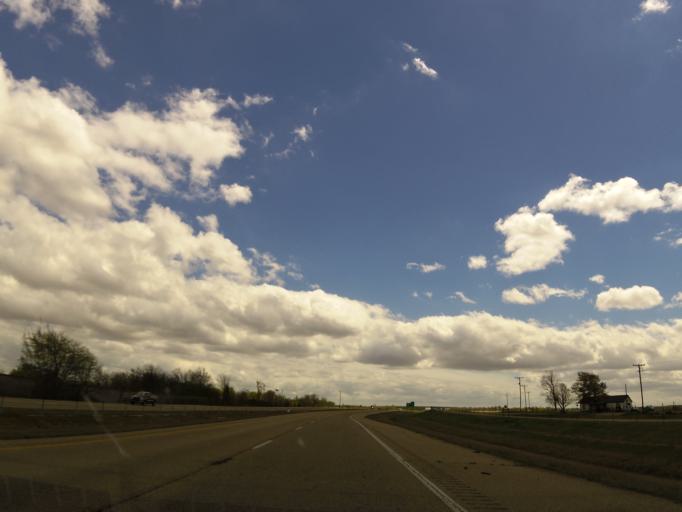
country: US
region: Arkansas
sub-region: Poinsett County
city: Marked Tree
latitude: 35.4182
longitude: -90.2864
